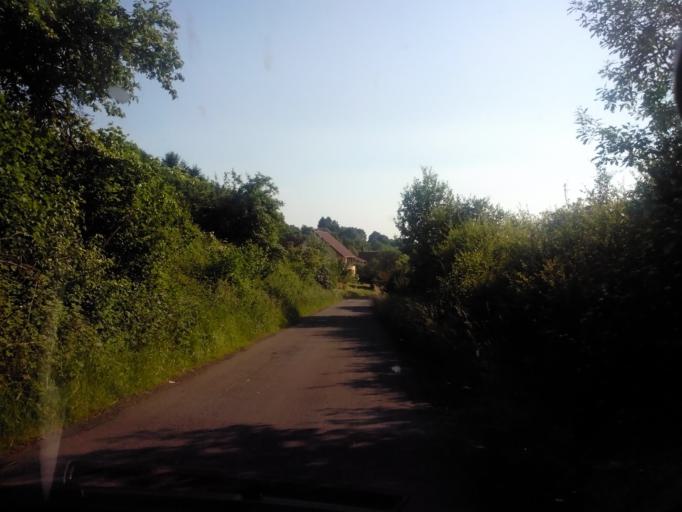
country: DE
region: Saarland
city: Nalbach
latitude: 49.4192
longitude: 6.7734
